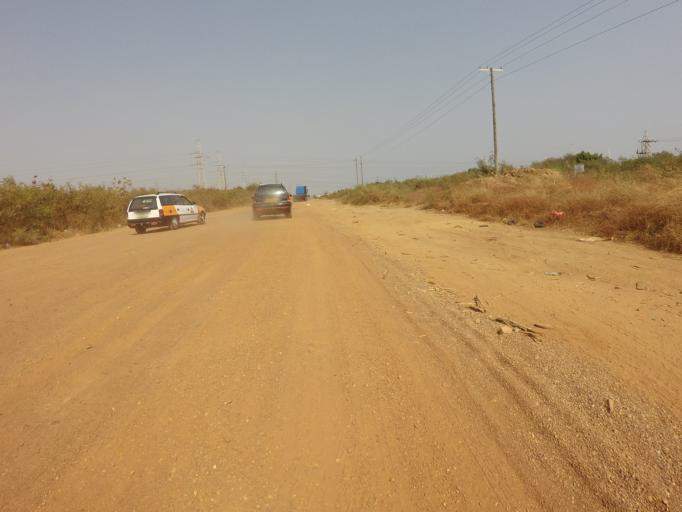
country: GH
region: Greater Accra
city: Tema
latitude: 5.6702
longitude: 0.0181
